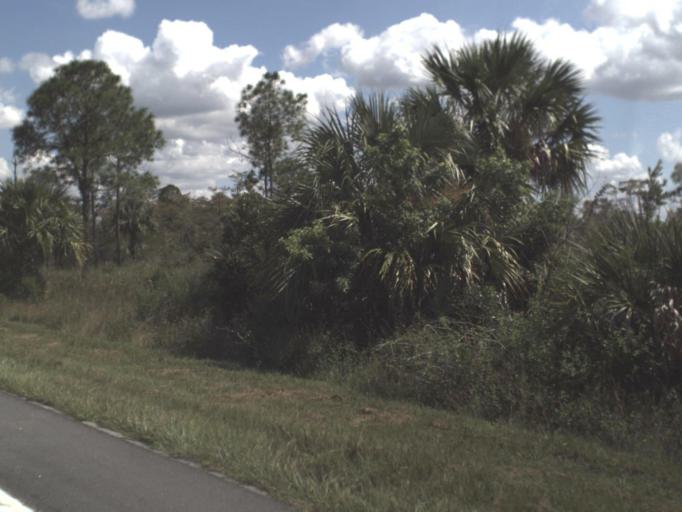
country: US
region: Florida
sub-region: Collier County
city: Lely Resort
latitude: 25.8654
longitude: -81.1170
